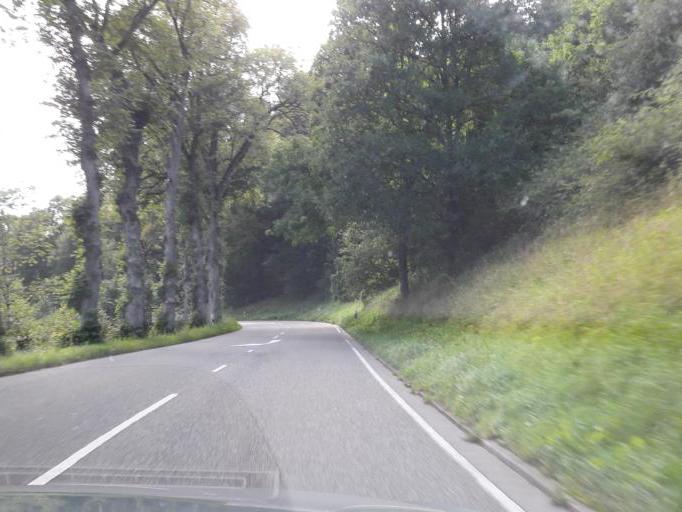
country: DE
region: Rheinland-Pfalz
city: Heimbach
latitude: 49.6162
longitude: 7.2583
